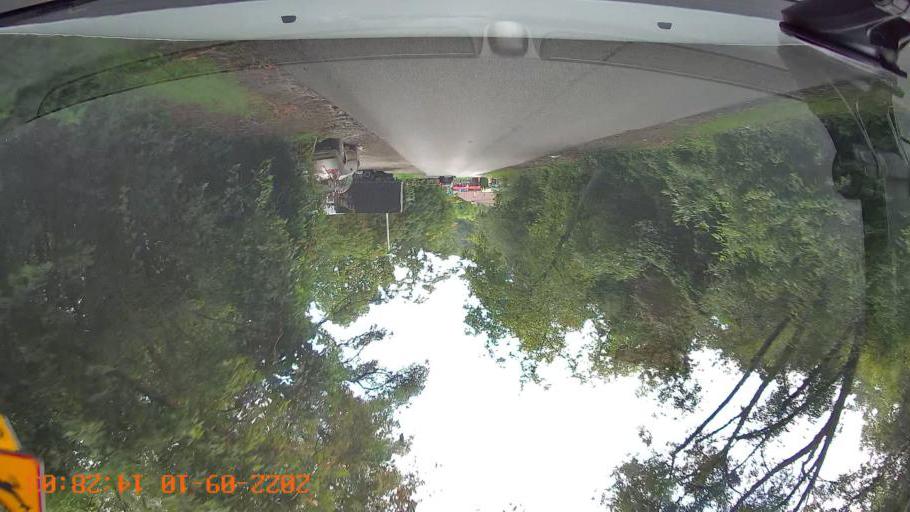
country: PL
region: Lesser Poland Voivodeship
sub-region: Powiat krakowski
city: Rzaska
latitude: 50.0690
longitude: 19.8468
